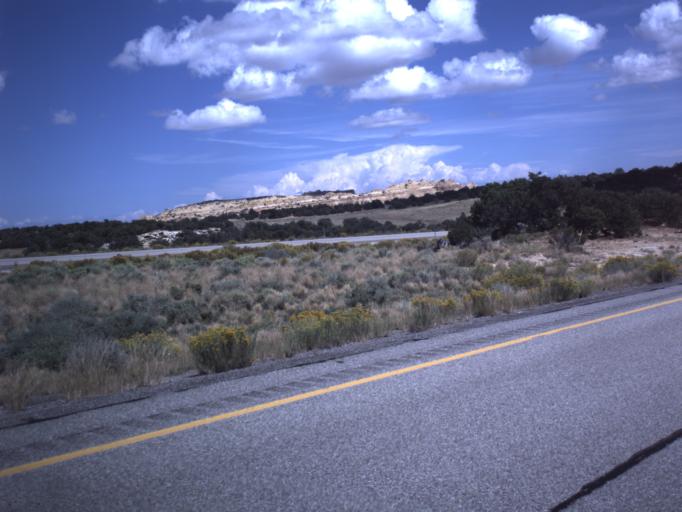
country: US
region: Utah
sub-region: Emery County
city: Ferron
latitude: 38.8661
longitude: -110.8038
